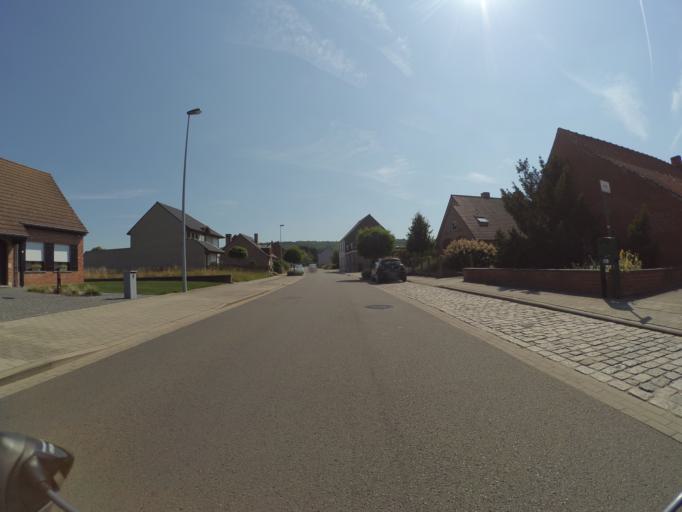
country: BE
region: Flanders
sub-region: Provincie West-Vlaanderen
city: Avelgem
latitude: 50.7698
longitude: 3.4836
